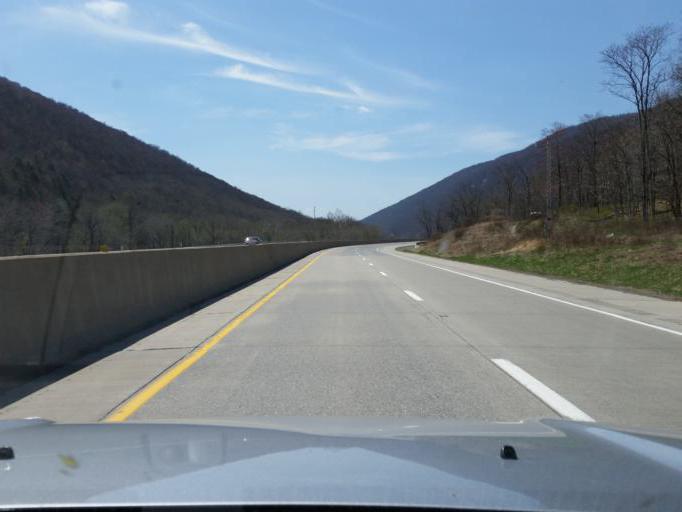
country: US
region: Pennsylvania
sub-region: Juniata County
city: Mifflintown
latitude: 40.6057
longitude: -77.4691
